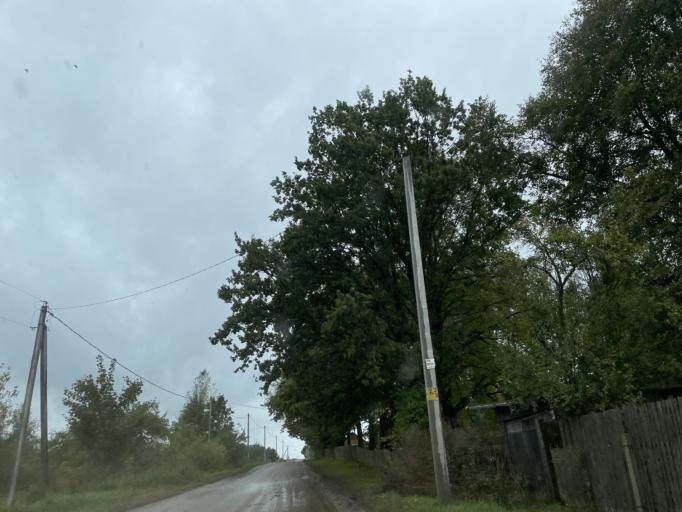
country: BY
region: Minsk
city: Snow
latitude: 53.2120
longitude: 26.2321
